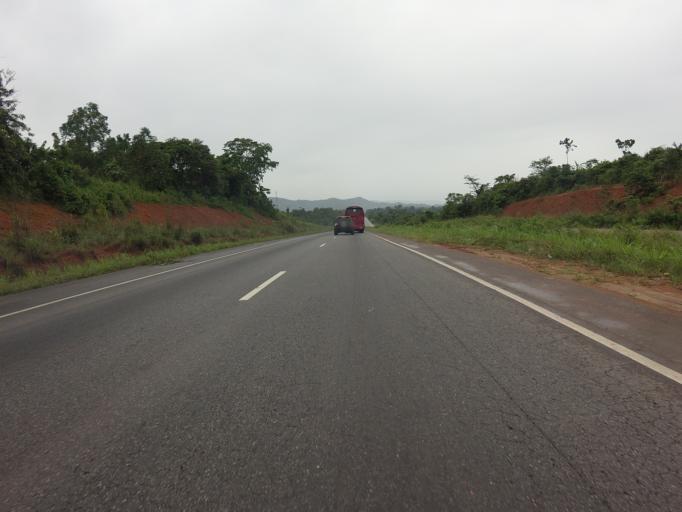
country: GH
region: Eastern
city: Suhum
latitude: 6.0782
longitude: -0.4722
